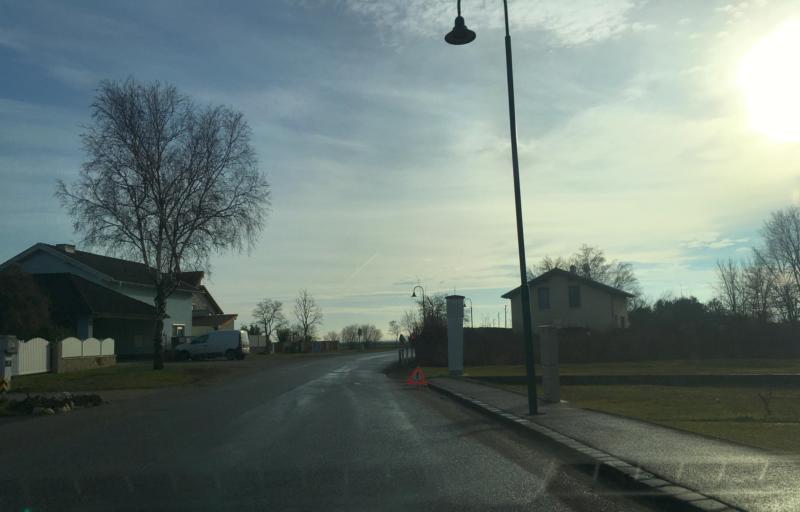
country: AT
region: Lower Austria
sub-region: Politischer Bezirk Ganserndorf
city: Glinzendorf
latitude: 48.2051
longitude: 16.6293
